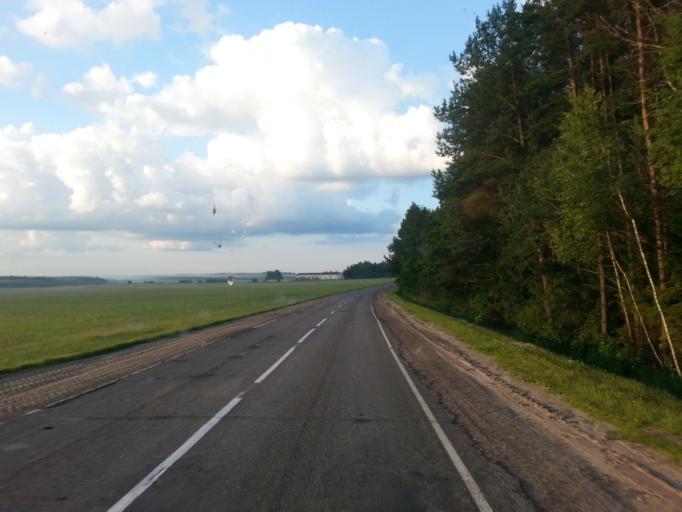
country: BY
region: Minsk
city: Il'ya
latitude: 54.5597
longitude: 27.2127
